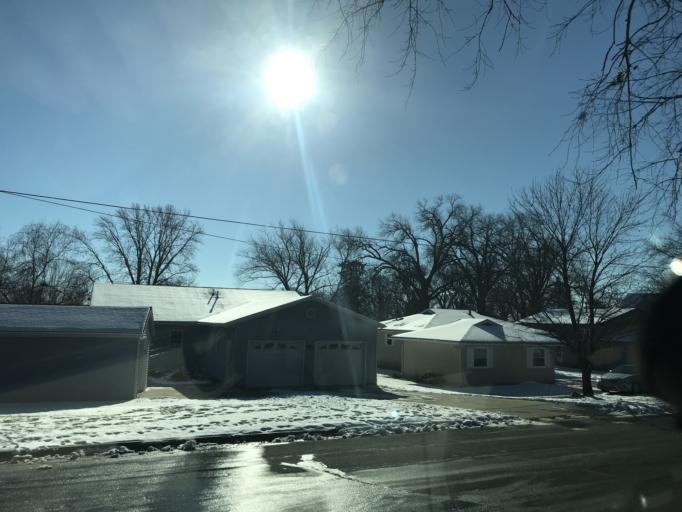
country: US
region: Wisconsin
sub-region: Dane County
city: Monona
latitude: 43.0493
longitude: -89.3337
